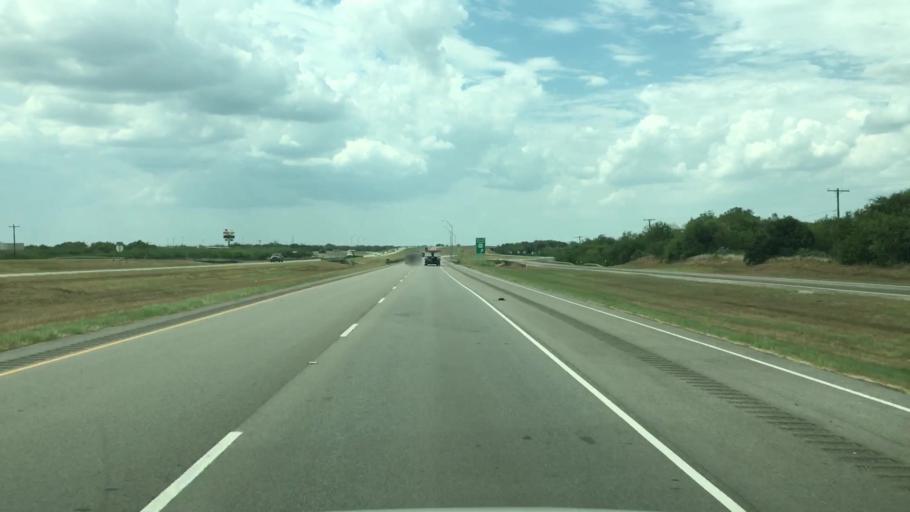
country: US
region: Texas
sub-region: Live Oak County
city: Three Rivers
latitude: 28.5171
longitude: -98.1764
